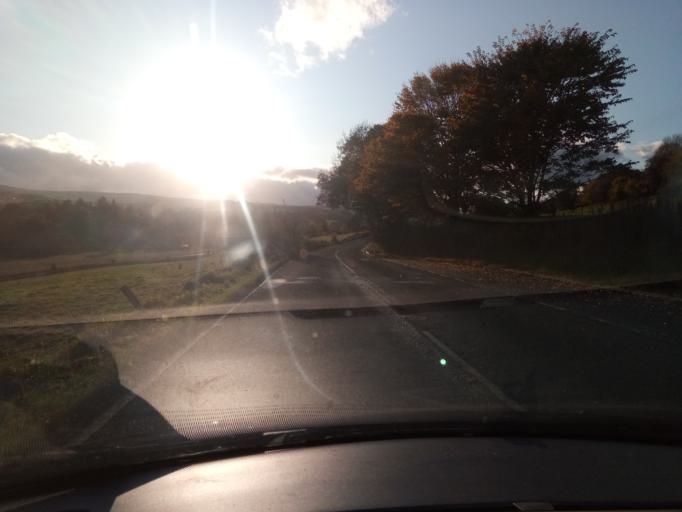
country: GB
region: England
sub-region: County Durham
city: Stanhope
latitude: 54.7464
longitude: -2.0338
